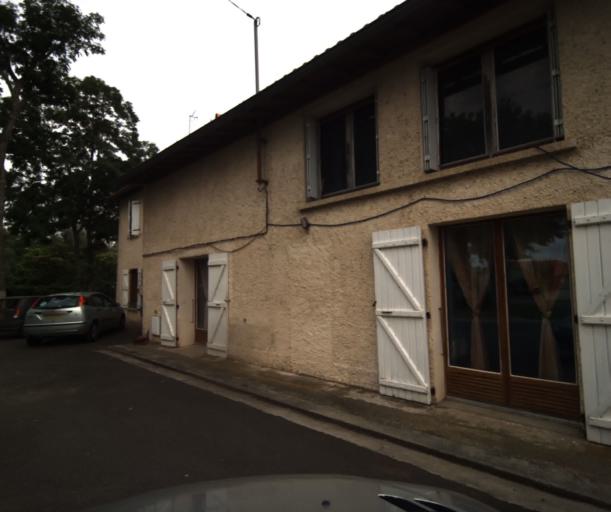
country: FR
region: Midi-Pyrenees
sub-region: Departement de la Haute-Garonne
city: Labarthe-sur-Leze
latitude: 43.4481
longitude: 1.4019
